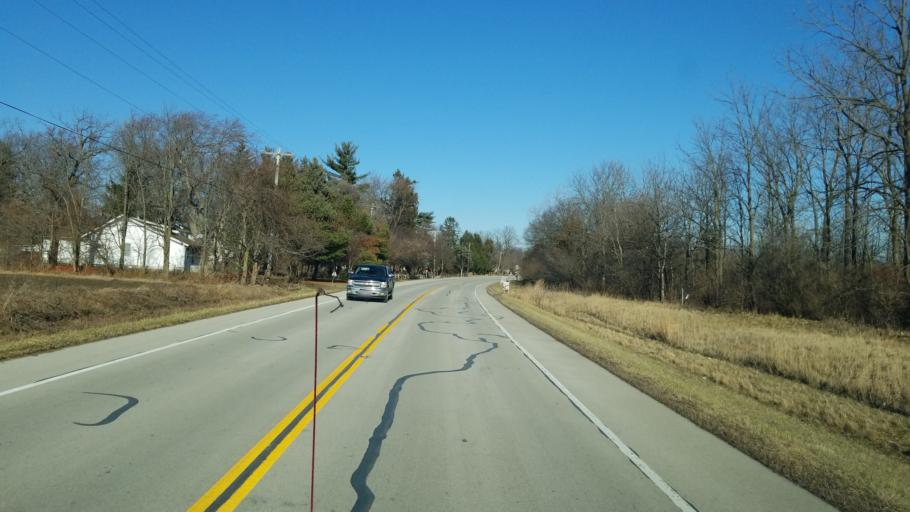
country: US
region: Ohio
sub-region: Lucas County
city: Whitehouse
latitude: 41.4595
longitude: -83.7825
